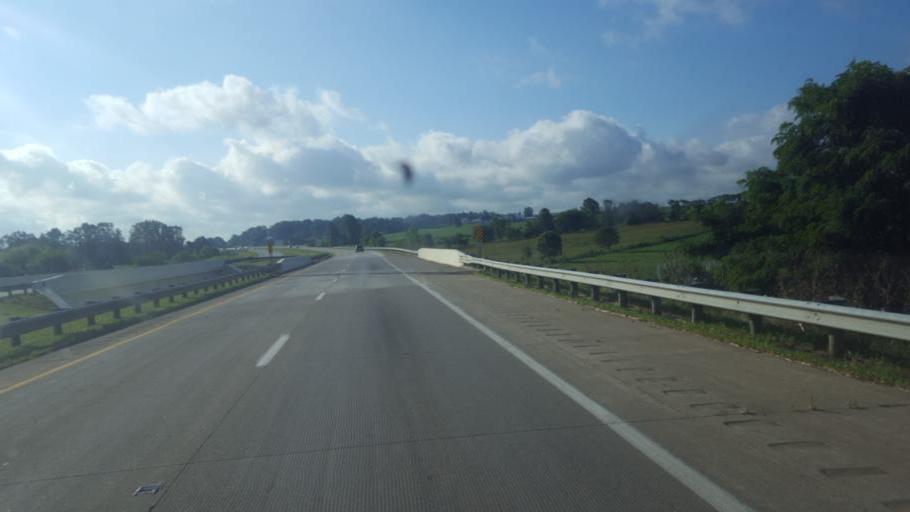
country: US
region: Ohio
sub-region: Wayne County
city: Apple Creek
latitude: 40.7961
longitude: -81.8122
